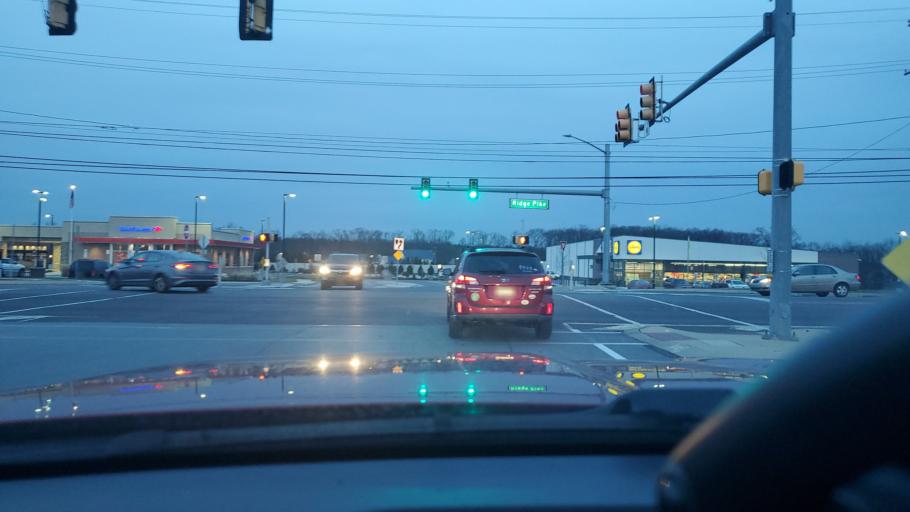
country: US
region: Pennsylvania
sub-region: Montgomery County
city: Trappe
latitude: 40.2130
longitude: -75.4971
